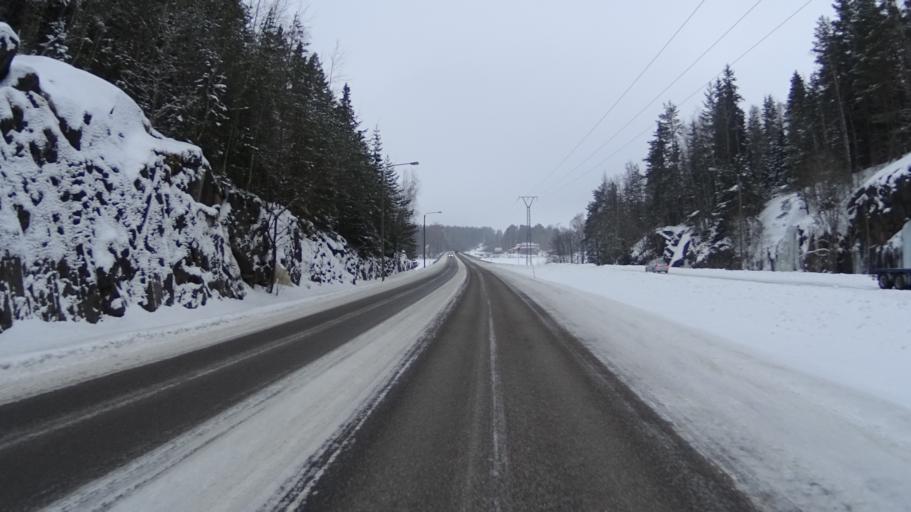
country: FI
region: Uusimaa
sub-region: Helsinki
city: Lohja
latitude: 60.3597
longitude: 24.1741
